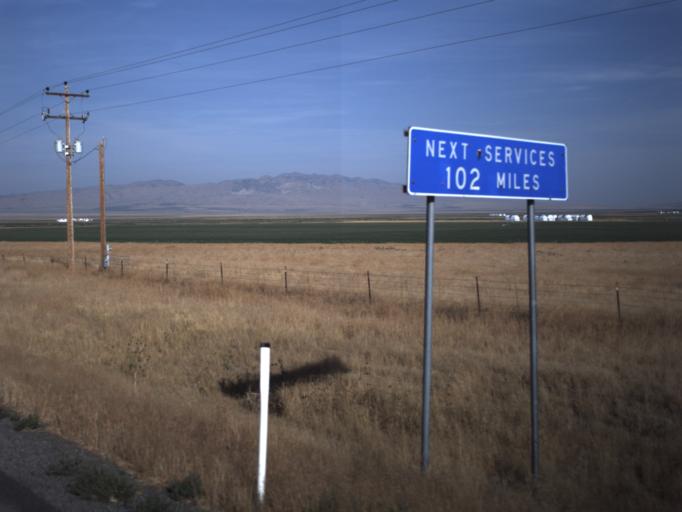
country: US
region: Idaho
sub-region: Oneida County
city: Malad City
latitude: 41.9675
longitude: -112.8144
